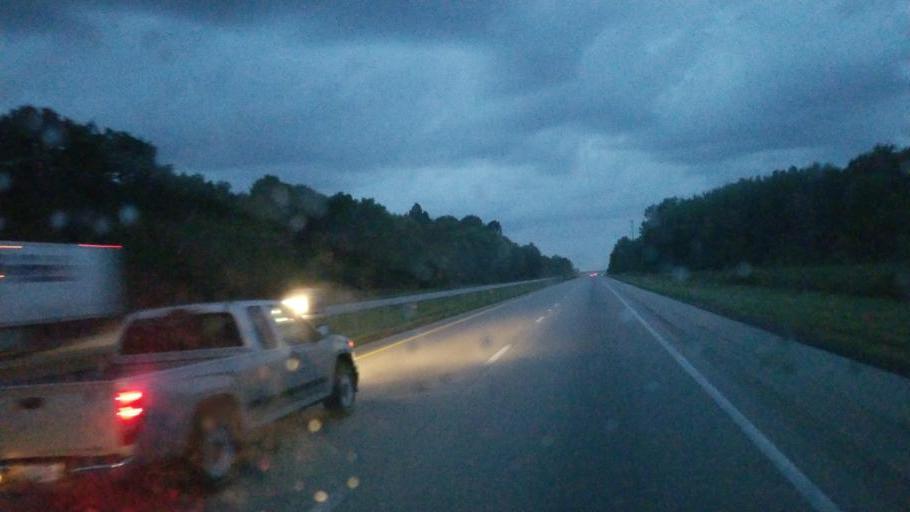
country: US
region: Ohio
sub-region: Medina County
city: Seville
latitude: 41.0322
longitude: -81.8211
